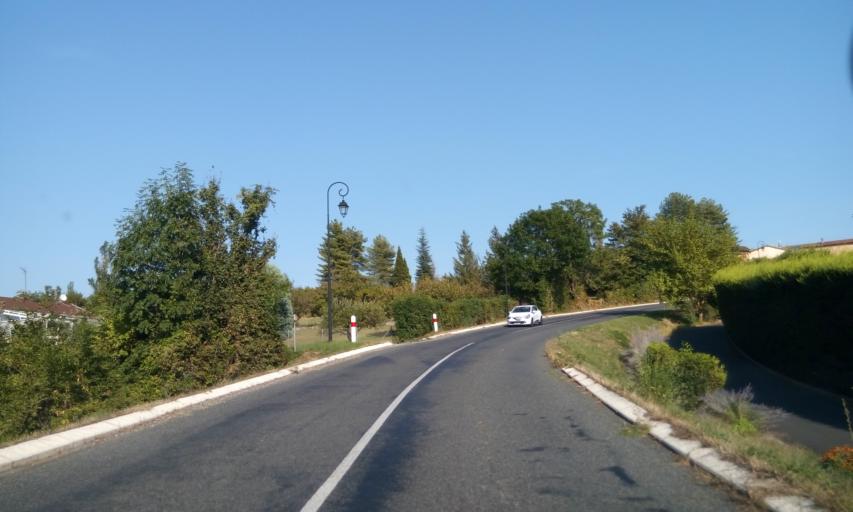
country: FR
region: Rhone-Alpes
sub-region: Departement du Rhone
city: Lucenay
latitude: 45.9262
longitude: 4.6759
